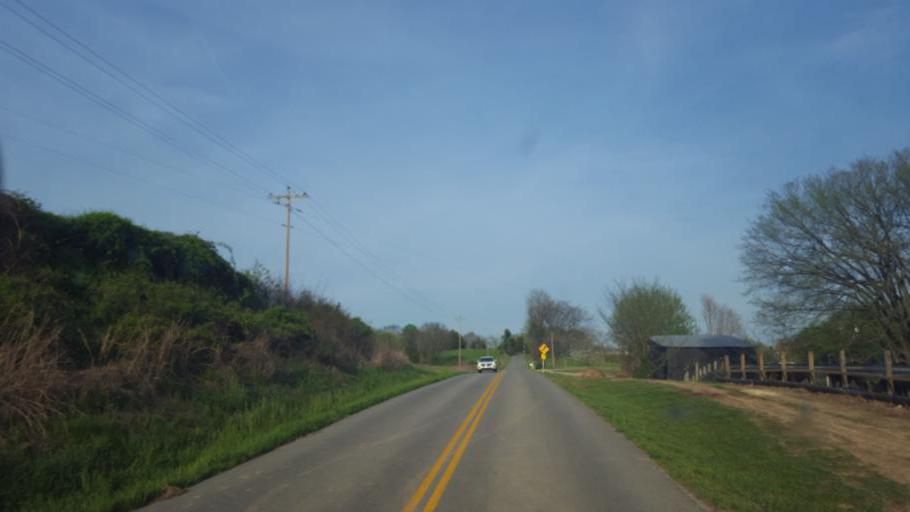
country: US
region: Kentucky
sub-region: Barren County
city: Glasgow
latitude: 36.9481
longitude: -86.0103
